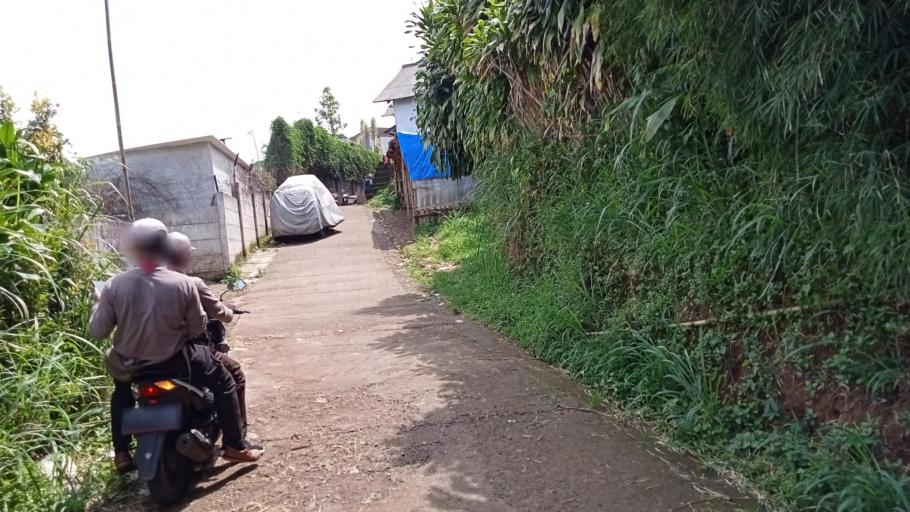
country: ID
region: West Java
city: Caringin
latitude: -6.6439
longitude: 106.9022
